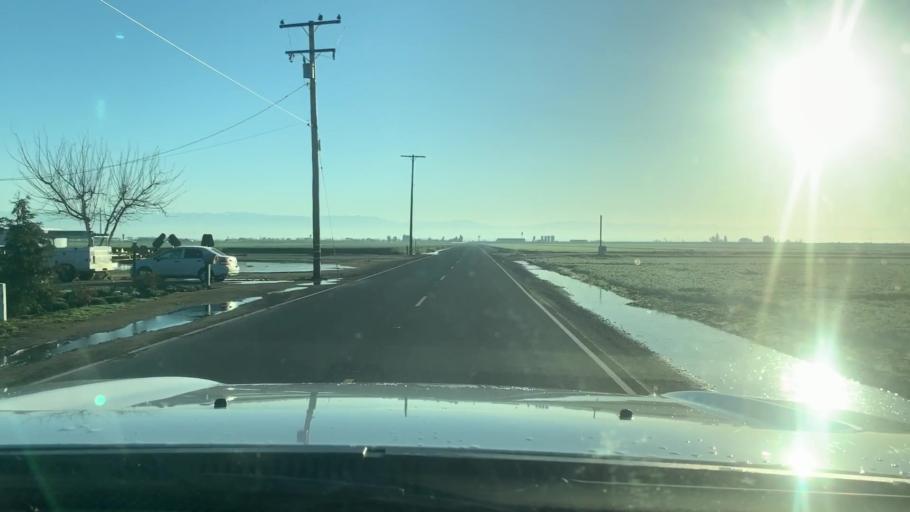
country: US
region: California
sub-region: Kings County
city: Corcoran
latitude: 36.2032
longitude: -119.4895
